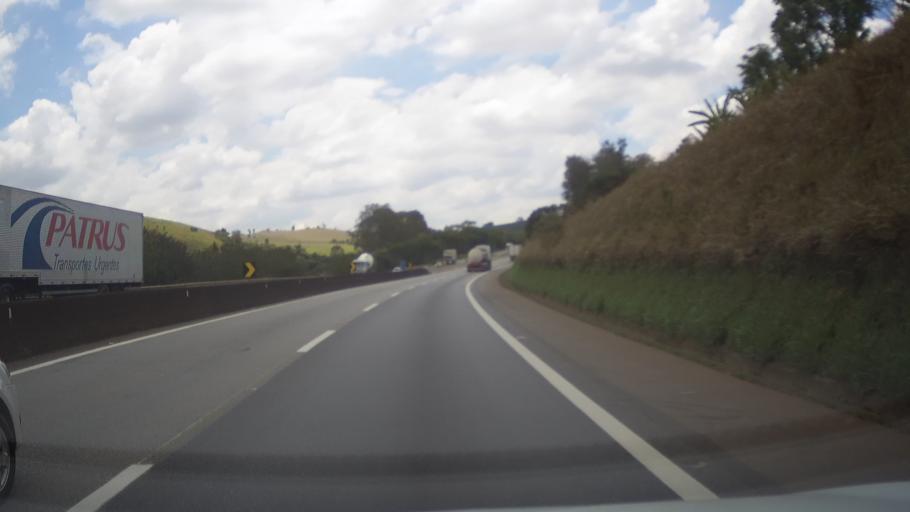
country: BR
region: Minas Gerais
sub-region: Tres Coracoes
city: Tres Coracoes
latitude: -21.7087
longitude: -45.3745
